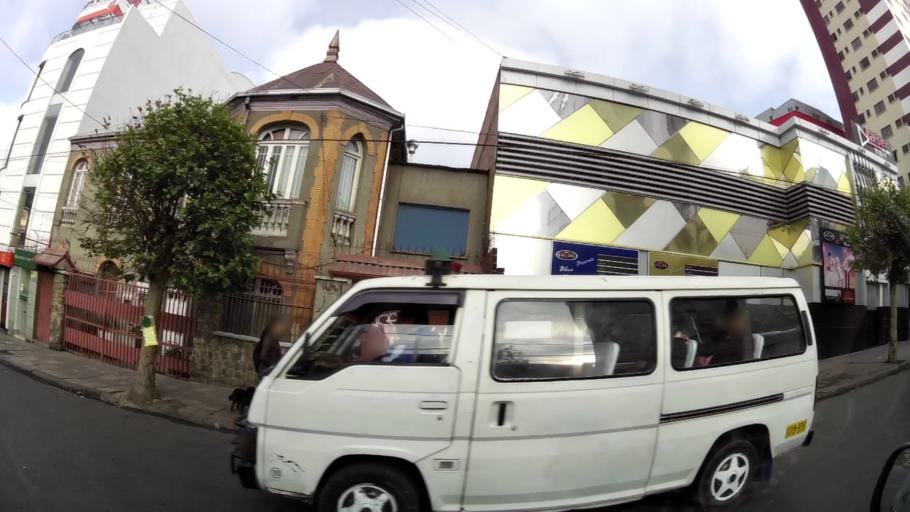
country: BO
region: La Paz
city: La Paz
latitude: -16.4987
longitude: -68.1243
